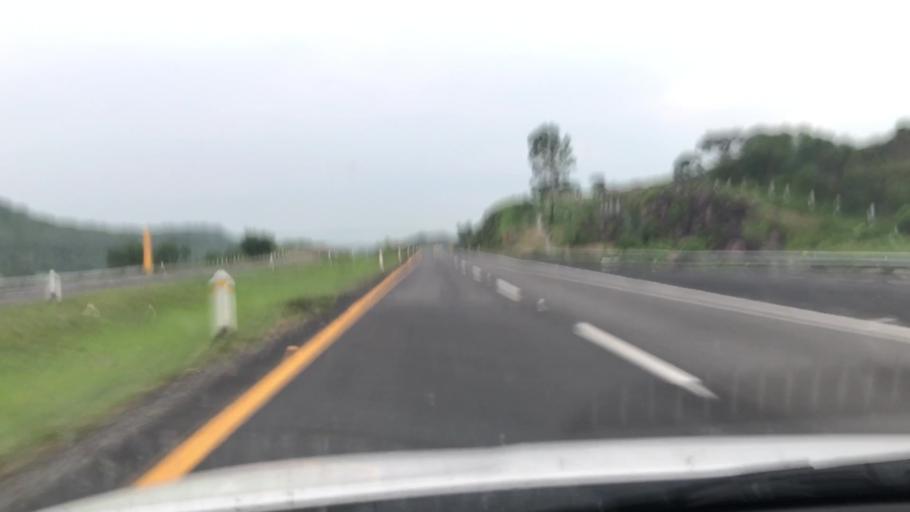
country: MX
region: Jalisco
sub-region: Zapotlan del Rey
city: Zapotlan del Rey
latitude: 20.5273
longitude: -103.0037
